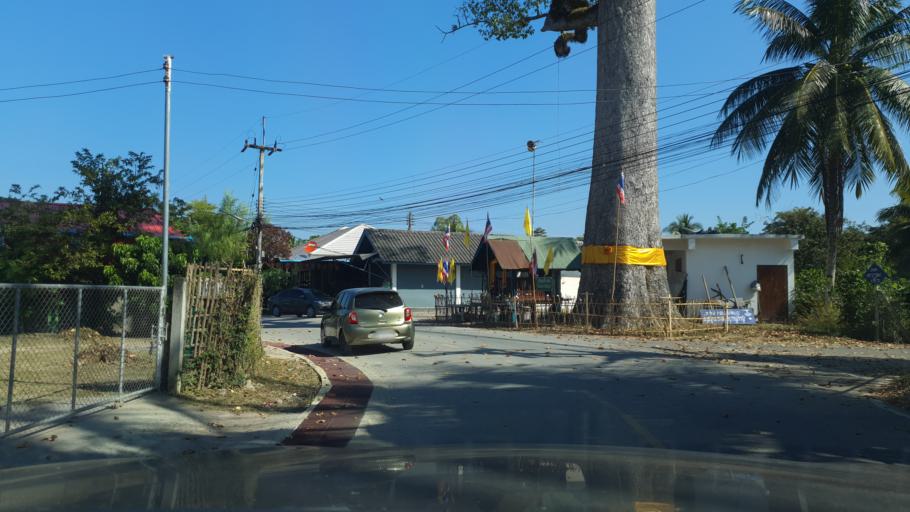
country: TH
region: Chiang Mai
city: San Sai
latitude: 18.8185
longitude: 99.0842
